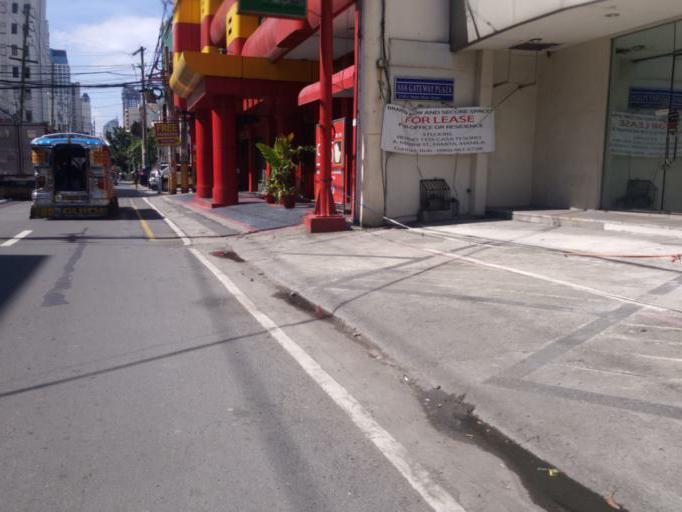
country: PH
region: Metro Manila
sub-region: City of Manila
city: Port Area
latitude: 14.5660
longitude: 120.9864
